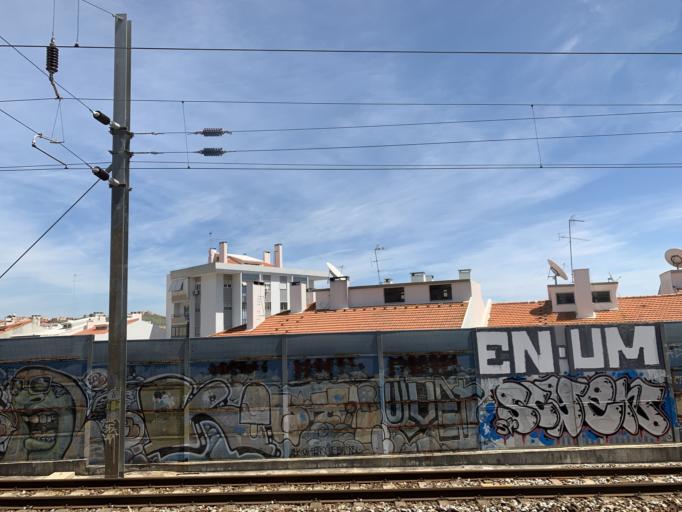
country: PT
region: Lisbon
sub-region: Amadora
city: Amadora
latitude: 38.7520
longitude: -9.2259
